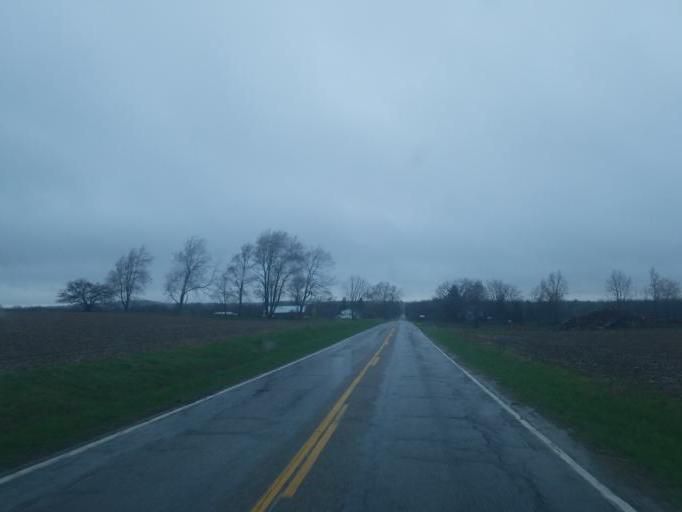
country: US
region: Michigan
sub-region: Montcalm County
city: Edmore
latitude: 43.4975
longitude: -85.0254
